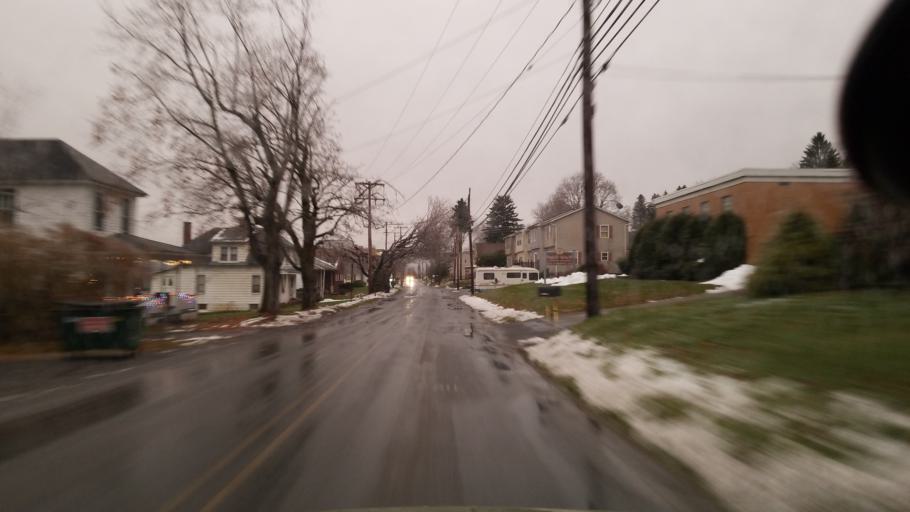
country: US
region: Pennsylvania
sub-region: Clearfield County
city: Clearfield
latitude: 41.0362
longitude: -78.4525
